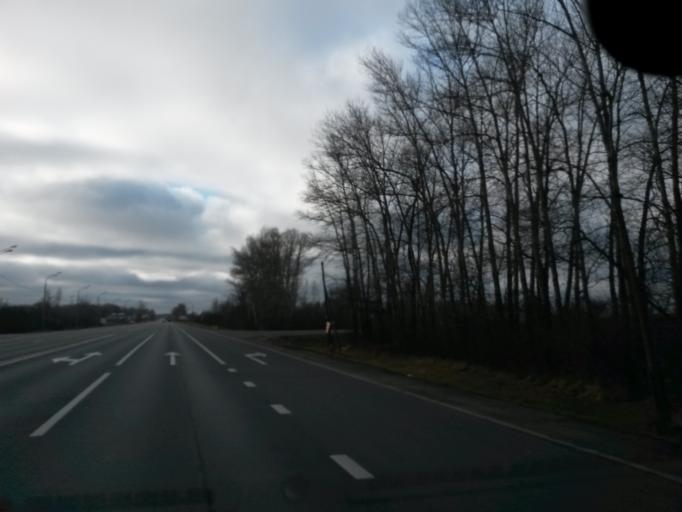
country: RU
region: Jaroslavl
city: Semibratovo
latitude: 57.3093
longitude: 39.5482
